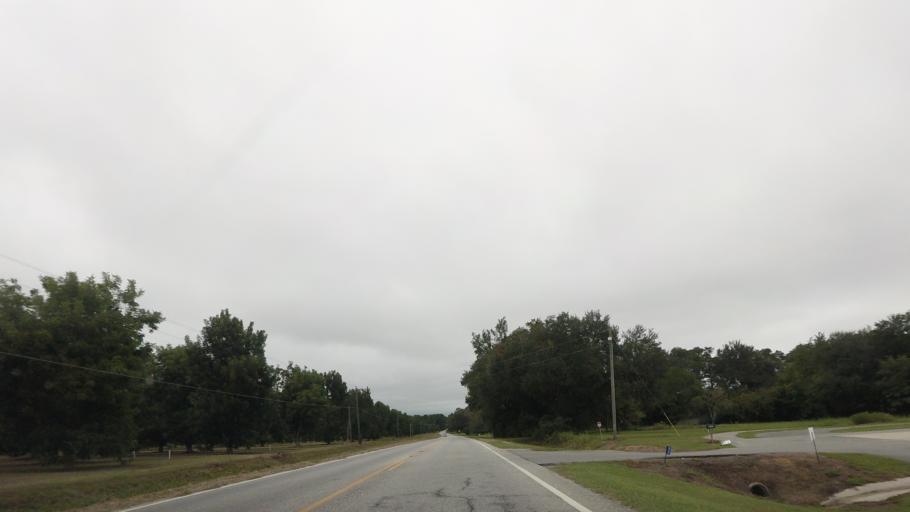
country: US
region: Georgia
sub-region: Berrien County
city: Ray City
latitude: 31.0423
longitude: -83.1977
